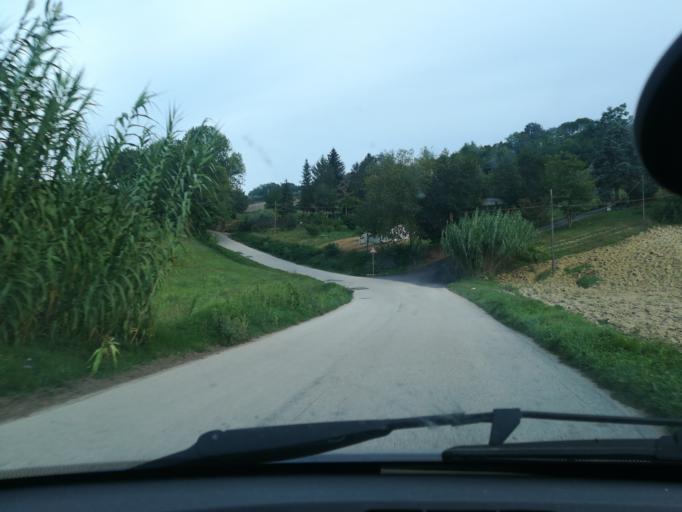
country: IT
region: The Marches
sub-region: Provincia di Macerata
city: Macerata
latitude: 43.3069
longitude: 13.4697
